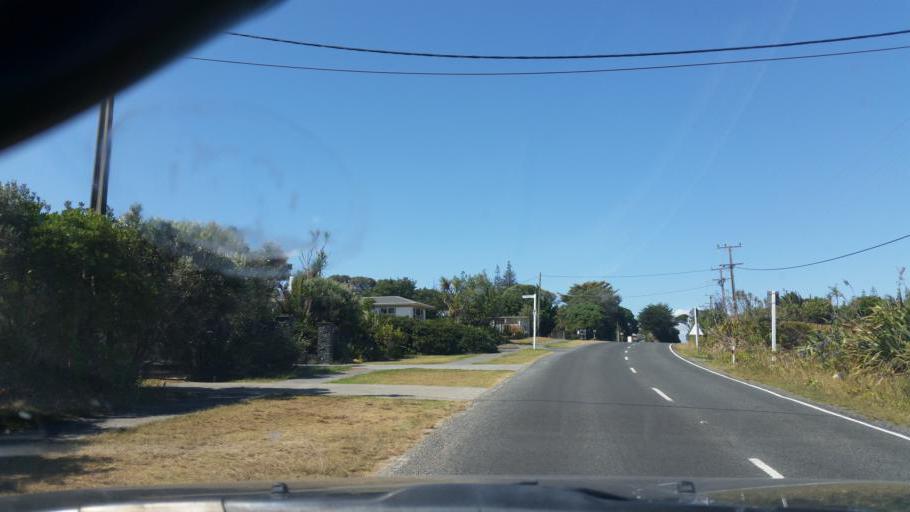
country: NZ
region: Northland
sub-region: Kaipara District
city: Dargaville
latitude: -35.9515
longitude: 173.7498
